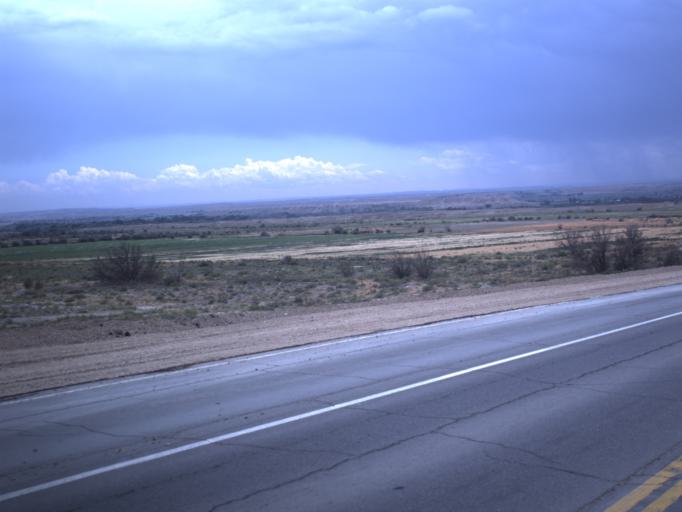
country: US
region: Utah
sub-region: Duchesne County
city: Roosevelt
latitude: 40.2318
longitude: -110.0675
